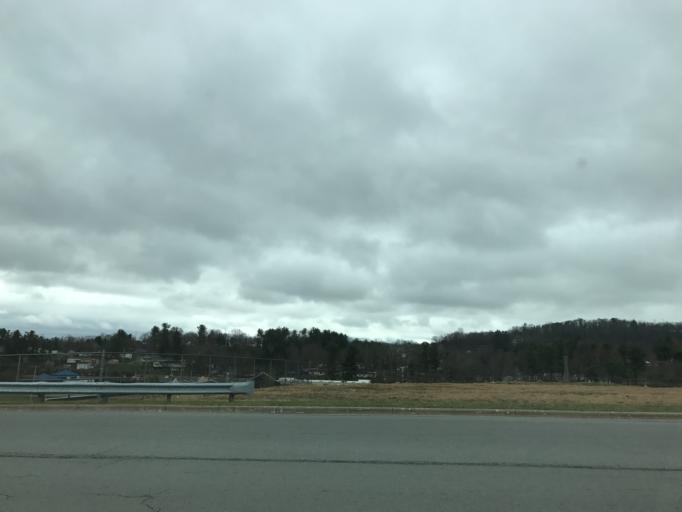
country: US
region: West Virginia
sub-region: Raleigh County
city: Beckley
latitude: 37.8004
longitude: -81.1744
